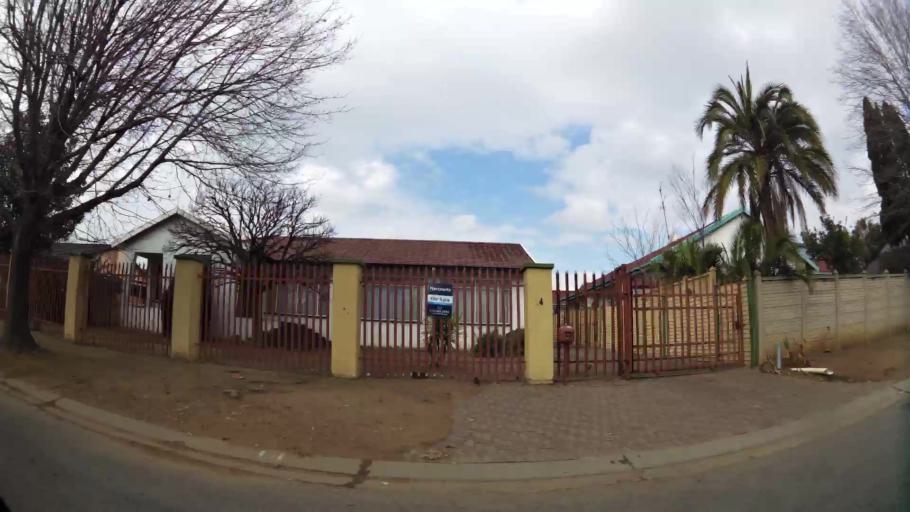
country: ZA
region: Gauteng
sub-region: Sedibeng District Municipality
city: Vanderbijlpark
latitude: -26.7139
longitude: 27.8600
